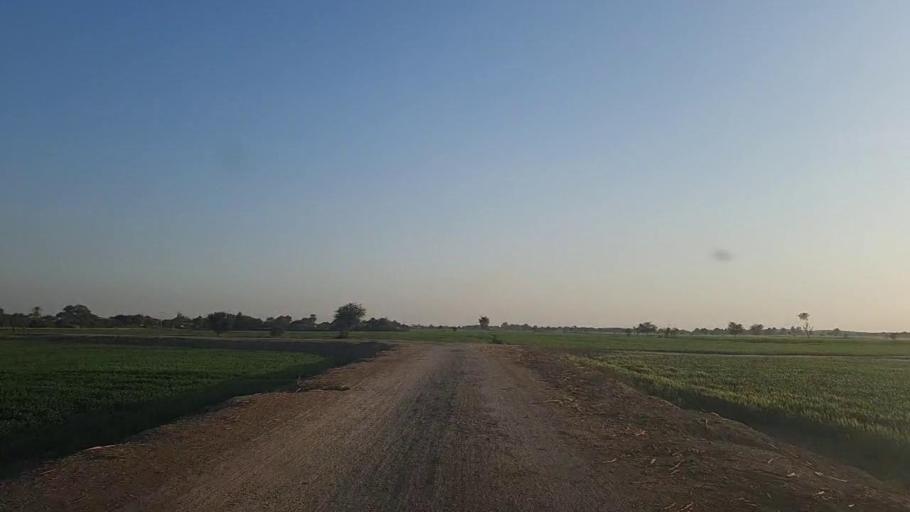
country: PK
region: Sindh
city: Jam Sahib
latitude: 26.3353
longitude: 68.6958
